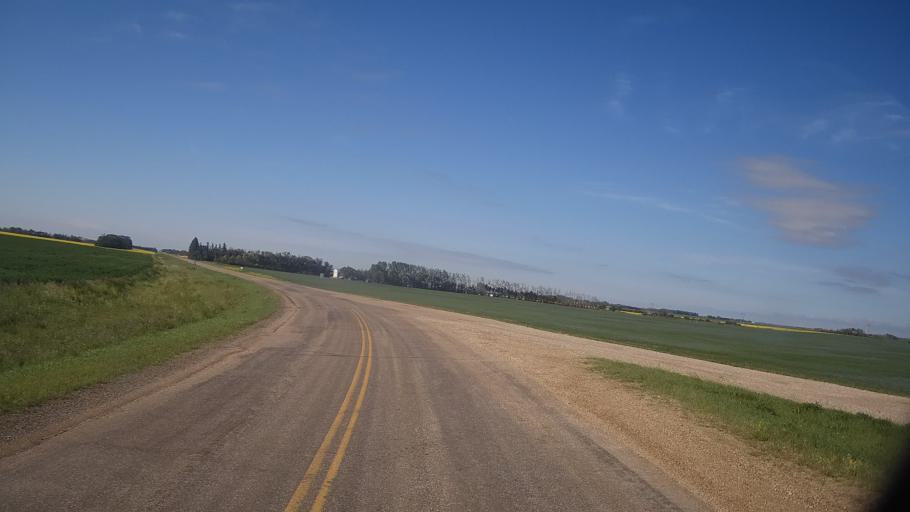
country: CA
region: Saskatchewan
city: Watrous
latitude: 51.8215
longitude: -105.2864
